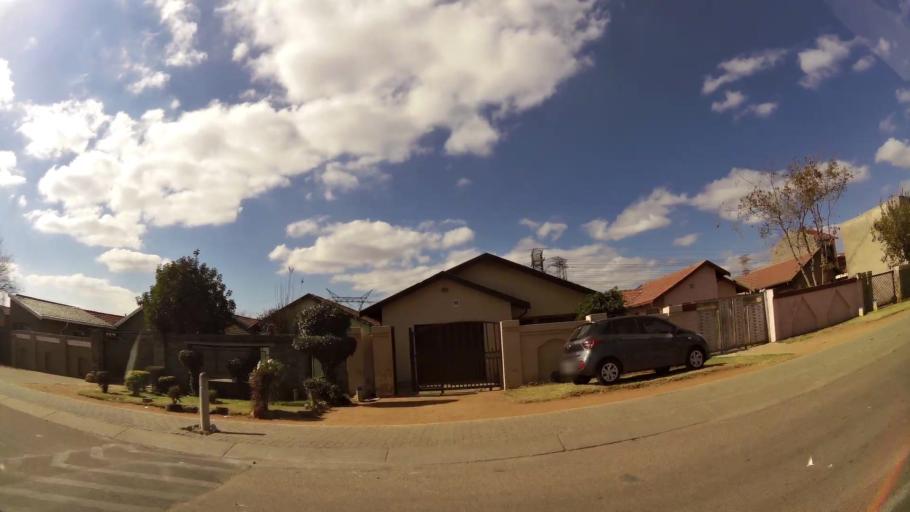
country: ZA
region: Gauteng
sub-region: City of Johannesburg Metropolitan Municipality
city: Modderfontein
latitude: -26.0315
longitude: 28.1766
